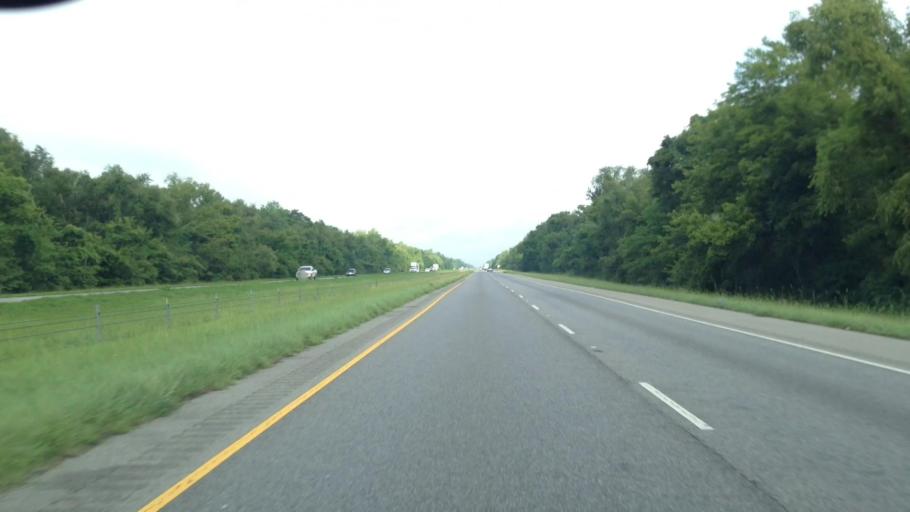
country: US
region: Louisiana
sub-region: Saint John the Baptist Parish
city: Garyville
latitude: 30.1147
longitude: -90.5841
